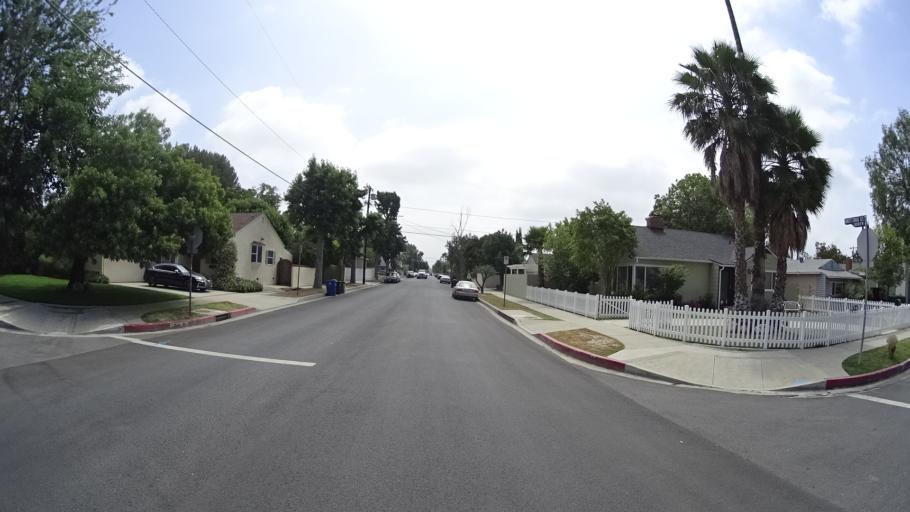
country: US
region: California
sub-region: Los Angeles County
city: Van Nuys
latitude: 34.1757
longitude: -118.4618
